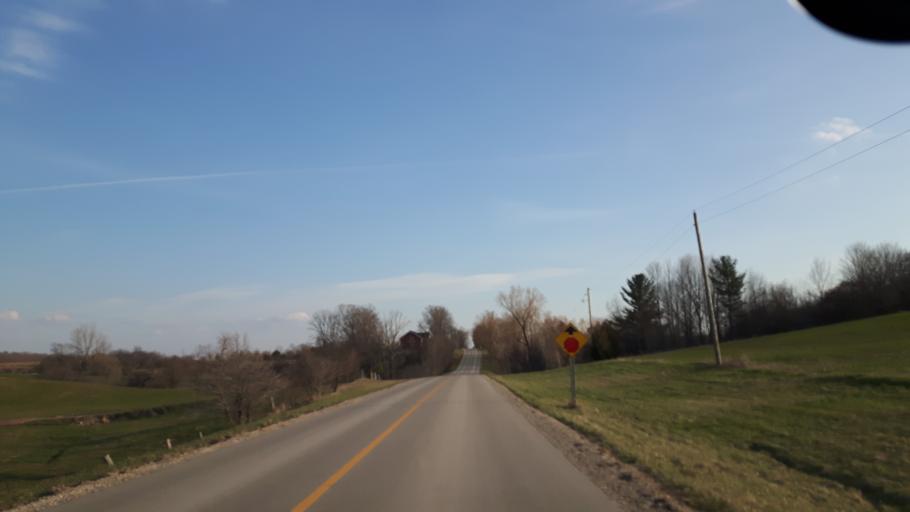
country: CA
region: Ontario
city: Goderich
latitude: 43.6461
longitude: -81.6643
